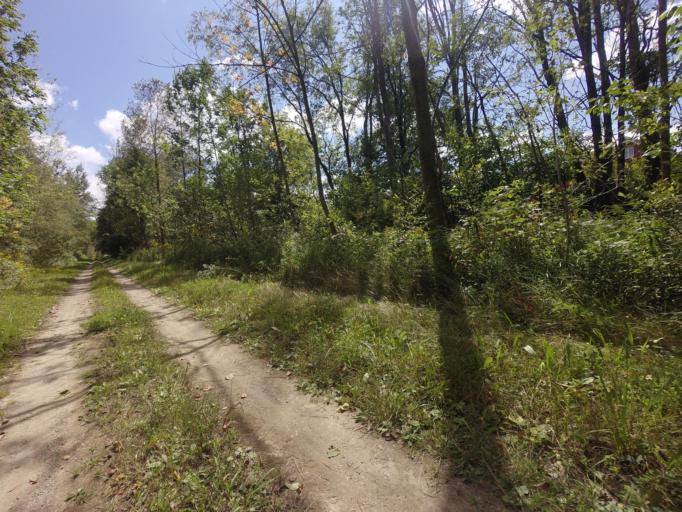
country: CA
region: Ontario
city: Orangeville
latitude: 43.7930
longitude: -80.2697
